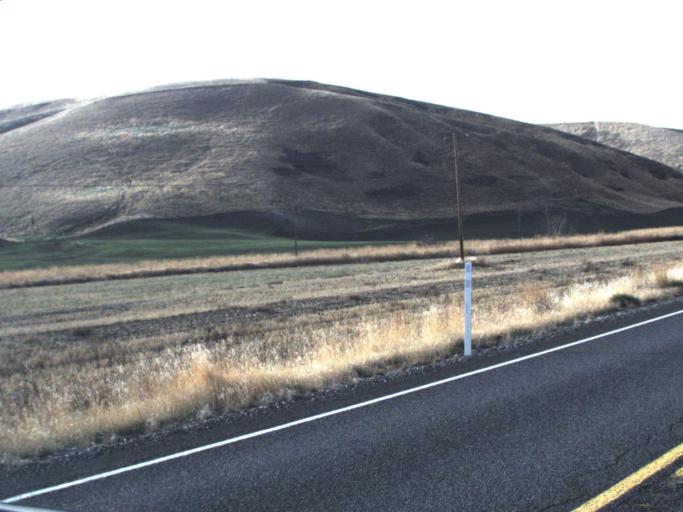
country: US
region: Washington
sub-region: Garfield County
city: Pomeroy
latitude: 46.4859
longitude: -117.7503
